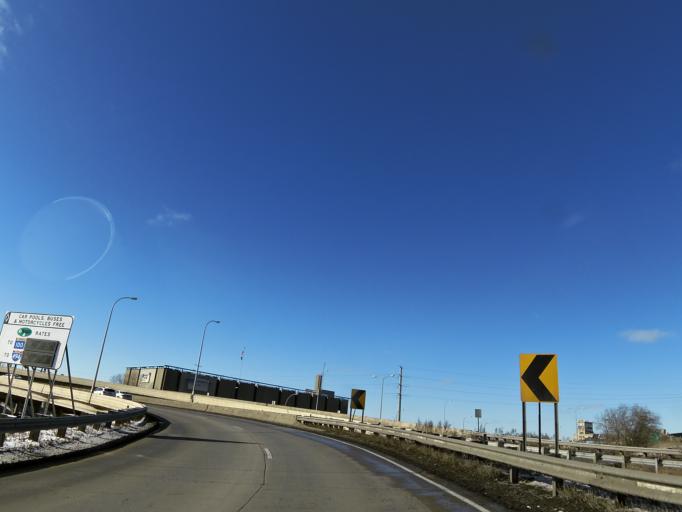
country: US
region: Minnesota
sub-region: Hennepin County
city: Minneapolis
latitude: 44.9757
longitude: -93.2870
